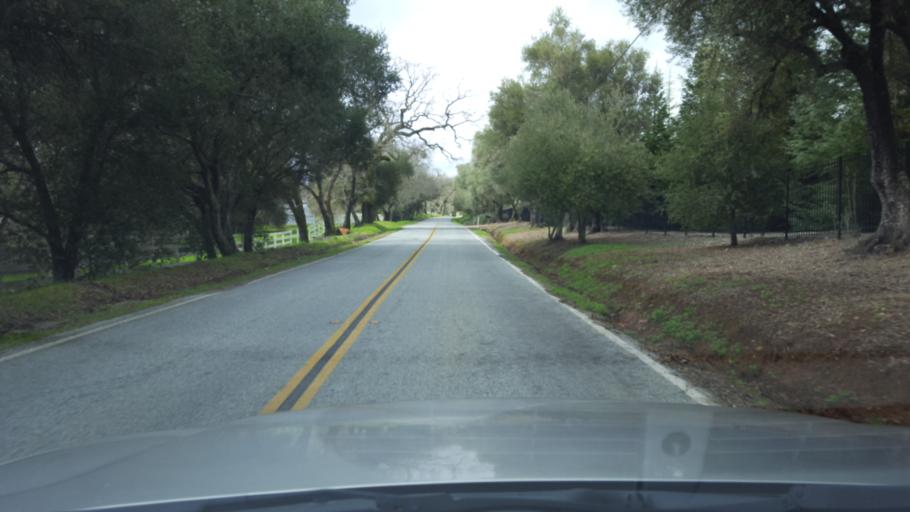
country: US
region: California
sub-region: Santa Clara County
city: San Martin
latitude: 37.0292
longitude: -121.6615
